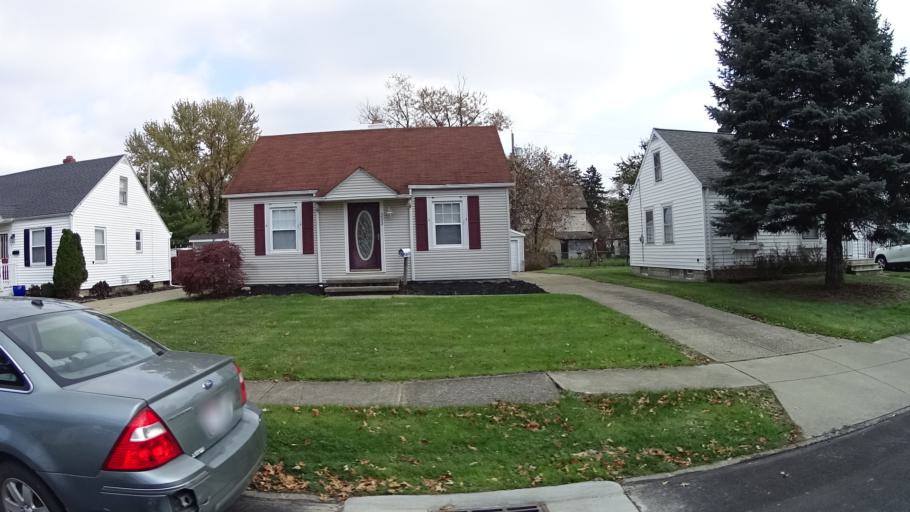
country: US
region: Ohio
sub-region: Lorain County
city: Elyria
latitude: 41.3789
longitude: -82.0804
